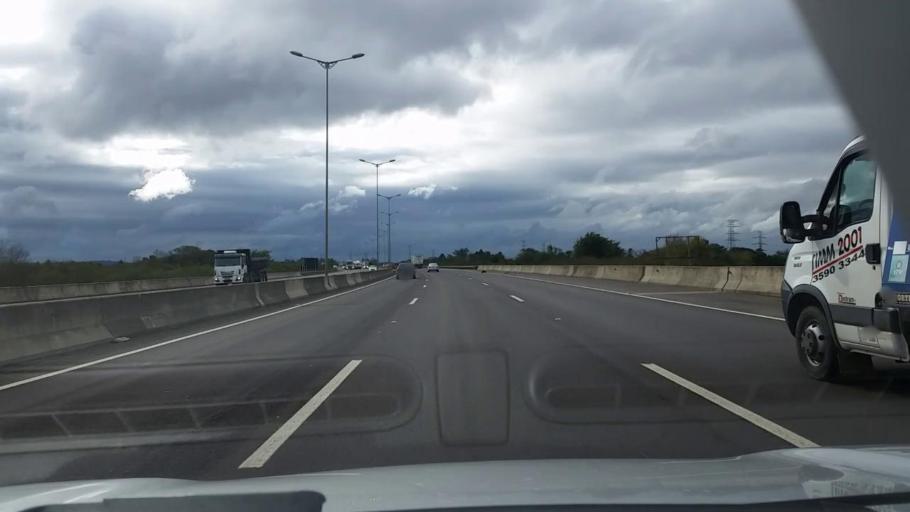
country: BR
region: Rio Grande do Sul
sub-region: Canoas
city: Canoas
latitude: -29.9419
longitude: -51.2051
